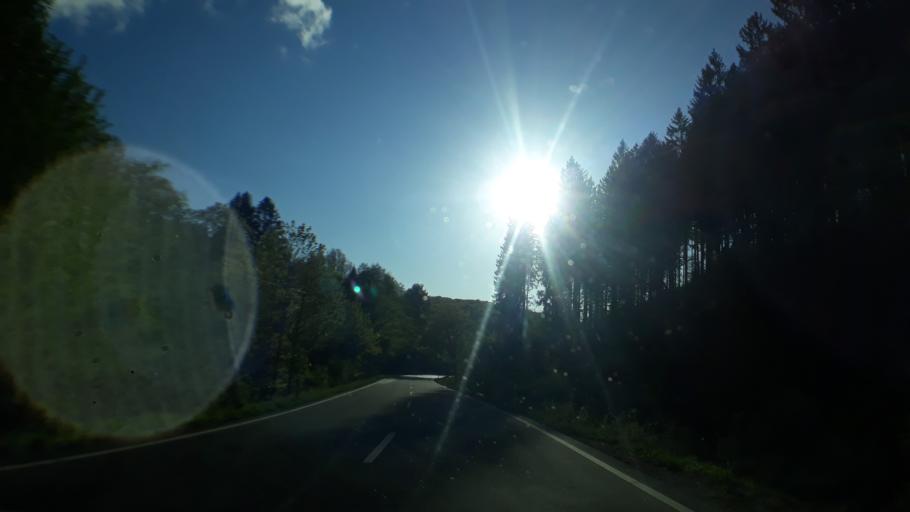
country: DE
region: North Rhine-Westphalia
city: Stolberg
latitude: 50.7098
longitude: 6.2783
